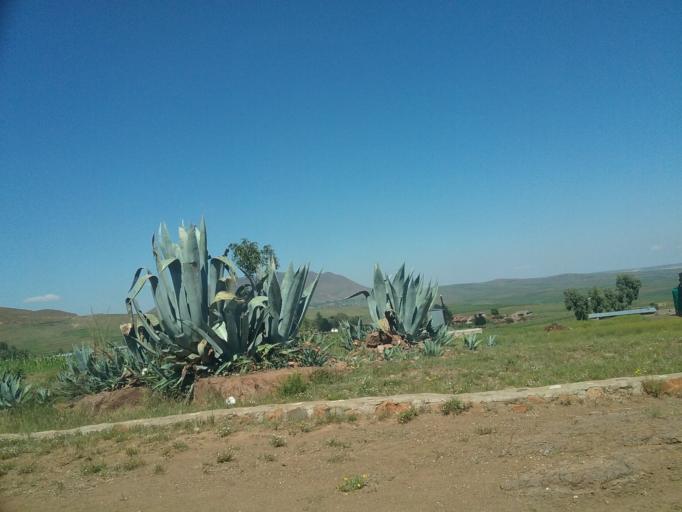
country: LS
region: Berea
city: Teyateyaneng
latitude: -29.2247
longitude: 27.8696
